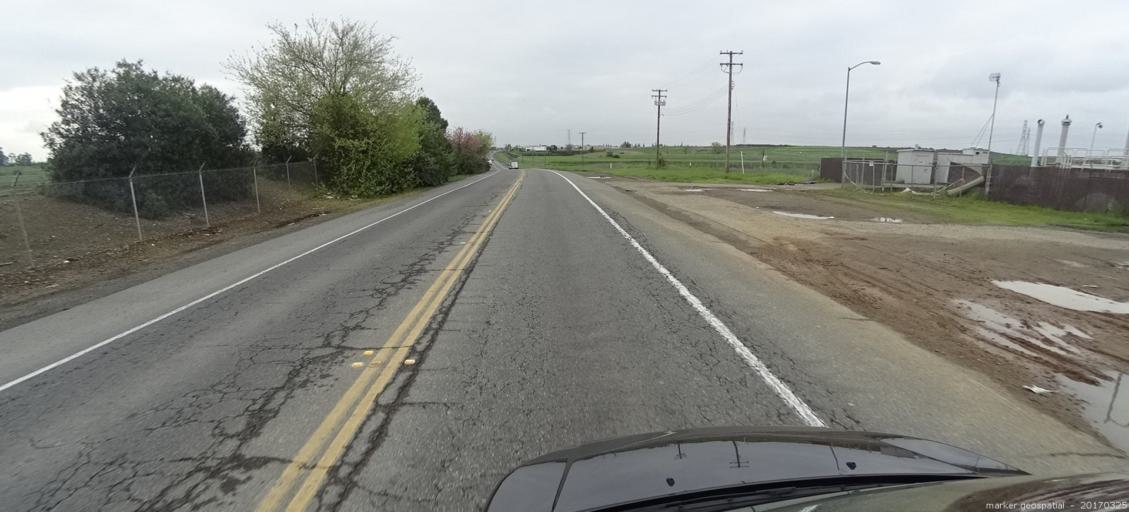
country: US
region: California
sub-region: Sacramento County
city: Rosemont
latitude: 38.5364
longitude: -121.3710
